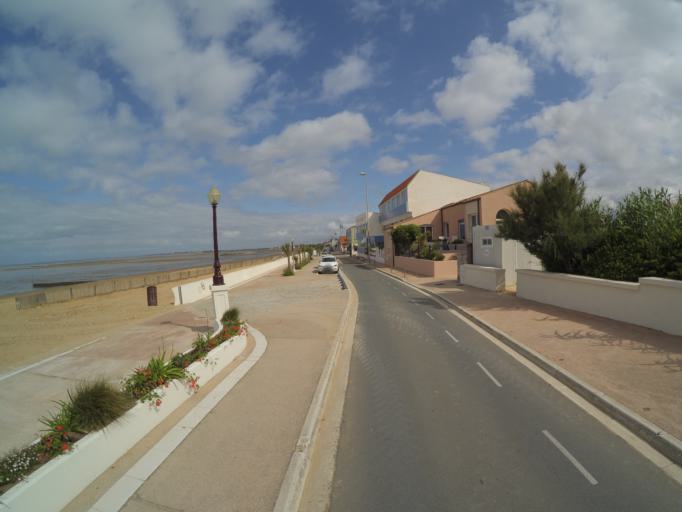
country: FR
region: Poitou-Charentes
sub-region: Departement de la Charente-Maritime
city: Chatelaillon-Plage
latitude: 46.0778
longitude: -1.0942
